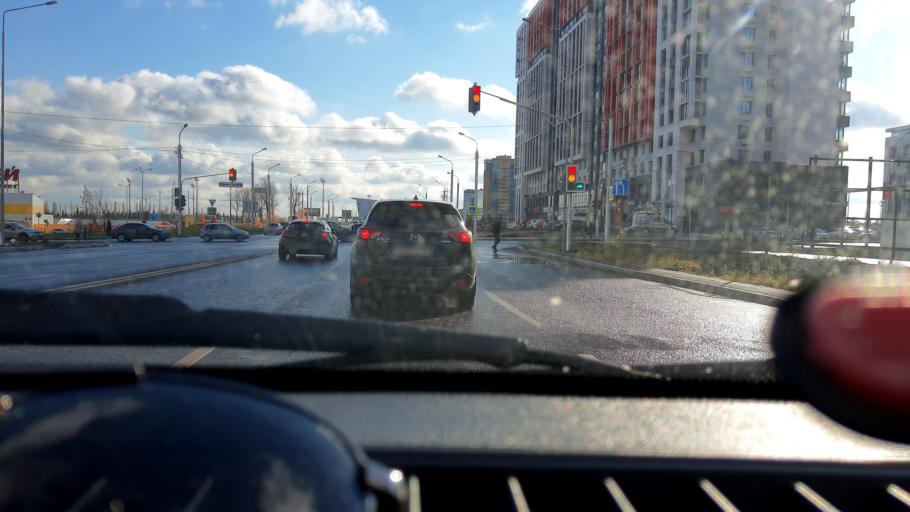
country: RU
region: Bashkortostan
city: Ufa
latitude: 54.7585
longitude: 56.0304
